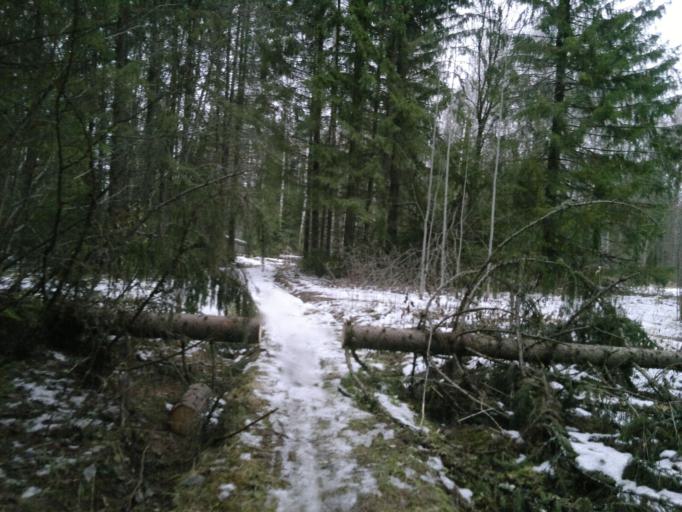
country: RU
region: Mariy-El
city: Yoshkar-Ola
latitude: 56.6036
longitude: 47.9602
